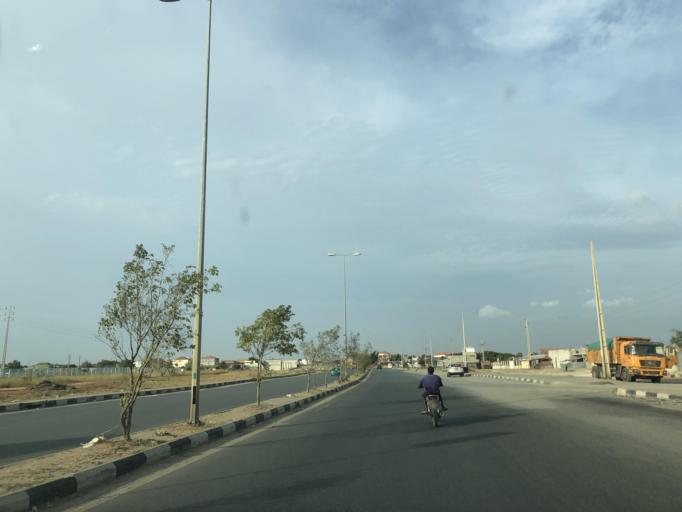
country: AO
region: Luanda
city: Luanda
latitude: -8.9326
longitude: 13.3010
